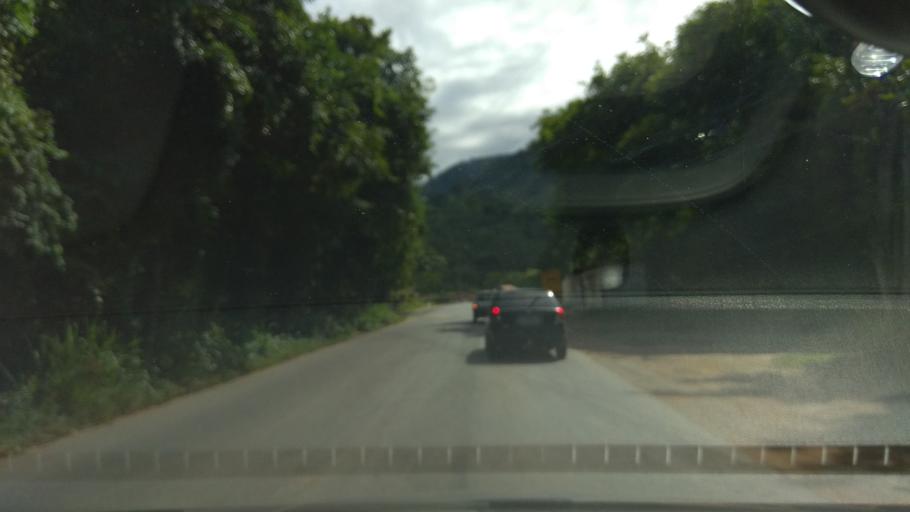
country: BR
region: Bahia
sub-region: Ubaira
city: Ubaira
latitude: -13.2593
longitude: -39.6175
